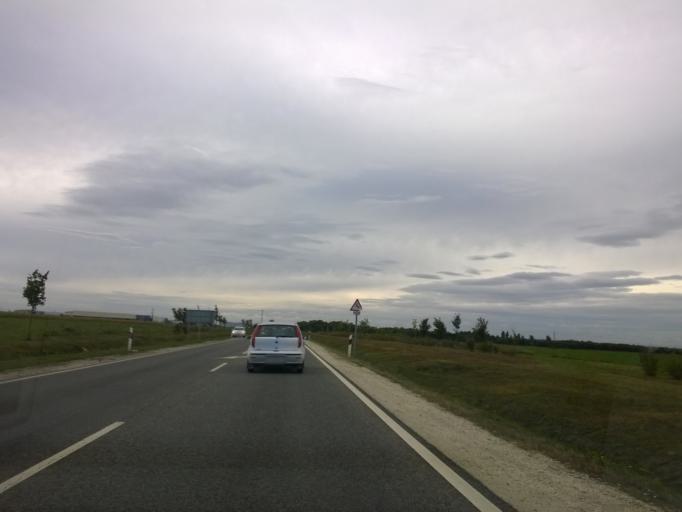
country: HU
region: Pest
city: Szigetszentmiklos
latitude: 47.3690
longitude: 19.0308
